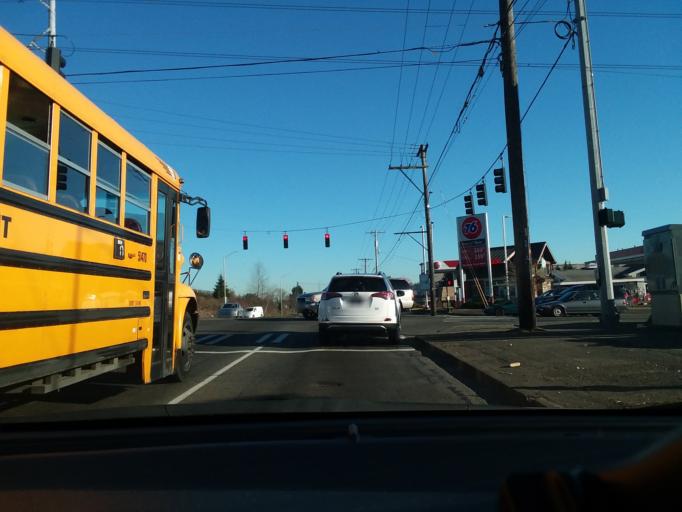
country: US
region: Washington
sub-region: Pierce County
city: Parkland
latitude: 47.1808
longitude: -122.4631
